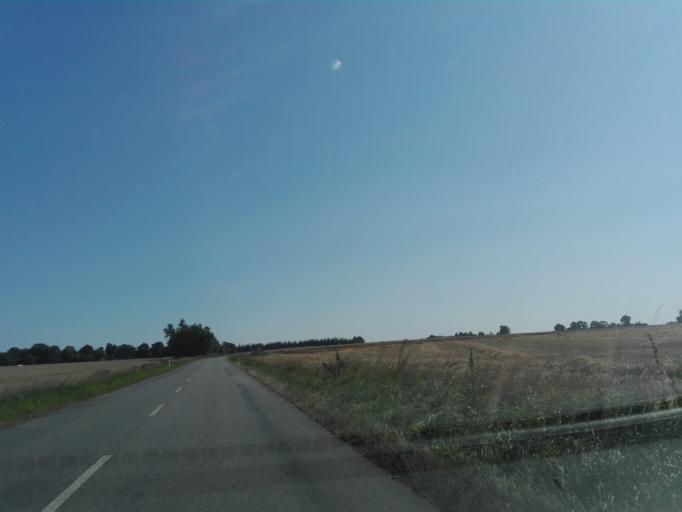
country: DK
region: Central Jutland
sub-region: Odder Kommune
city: Odder
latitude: 55.9596
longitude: 10.2348
